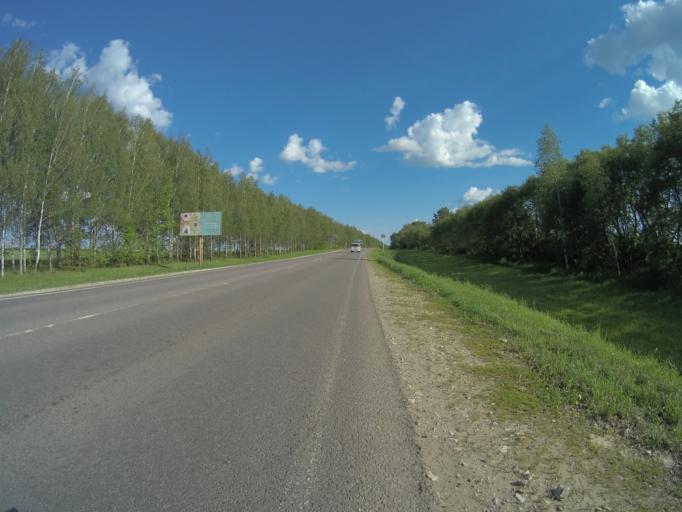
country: RU
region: Vladimir
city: Suzdal'
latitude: 56.3986
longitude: 40.4487
